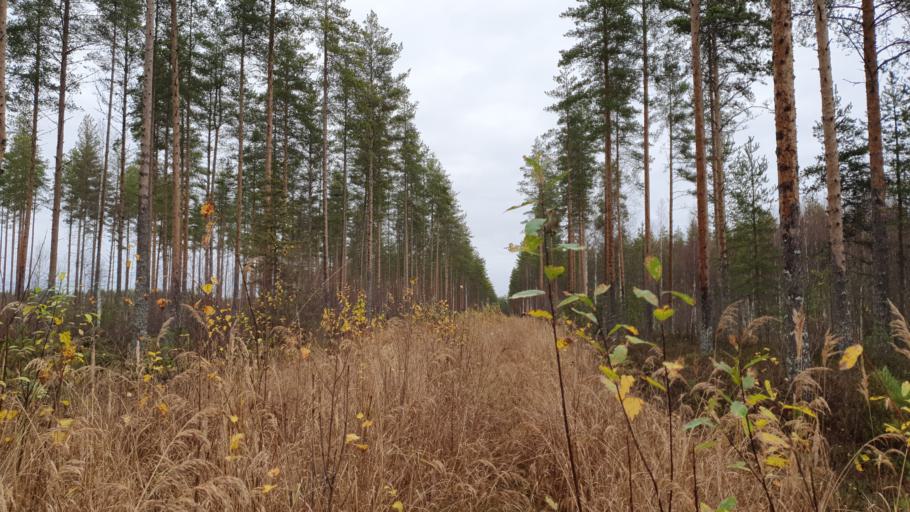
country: FI
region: Kainuu
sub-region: Kehys-Kainuu
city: Kuhmo
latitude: 64.1391
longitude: 29.4162
